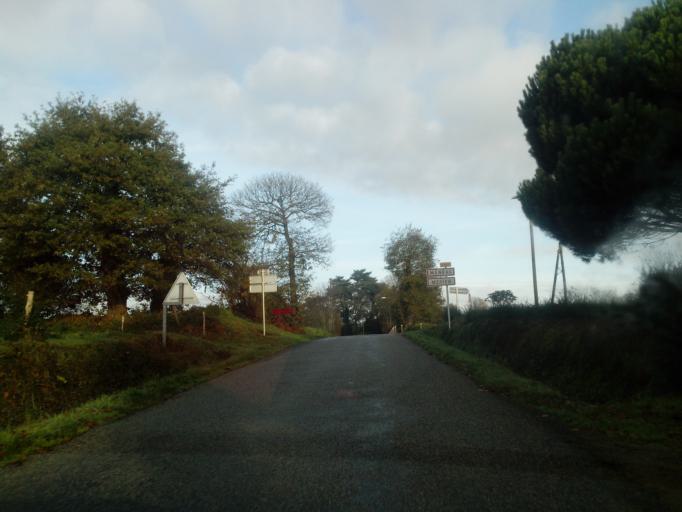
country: FR
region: Brittany
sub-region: Departement du Morbihan
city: Meneac
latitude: 48.1345
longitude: -2.4547
